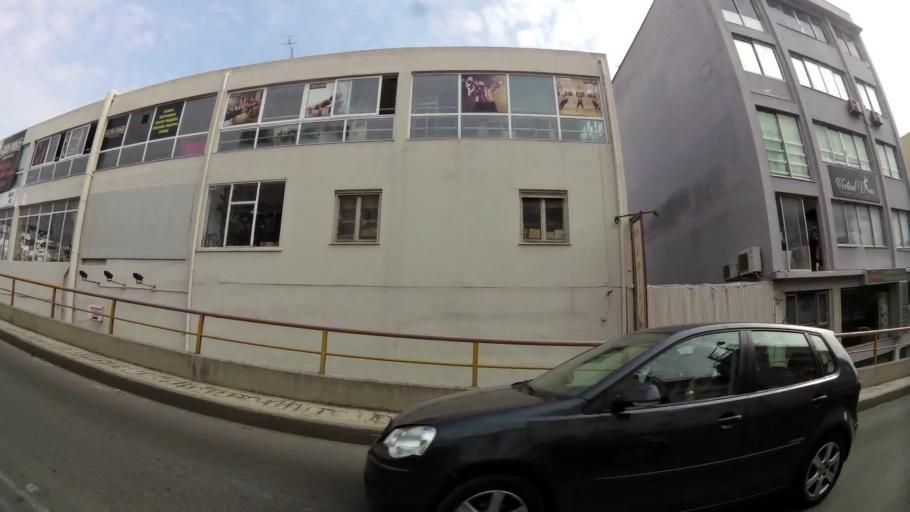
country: GR
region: Attica
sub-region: Nomarchia Athinas
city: Kallithea
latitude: 37.9602
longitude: 23.6978
